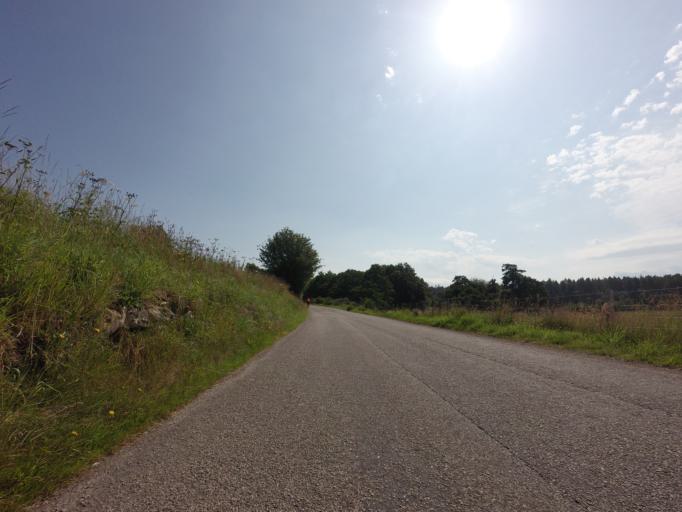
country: GB
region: Scotland
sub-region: Highland
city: Invergordon
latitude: 57.7550
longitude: -4.1423
